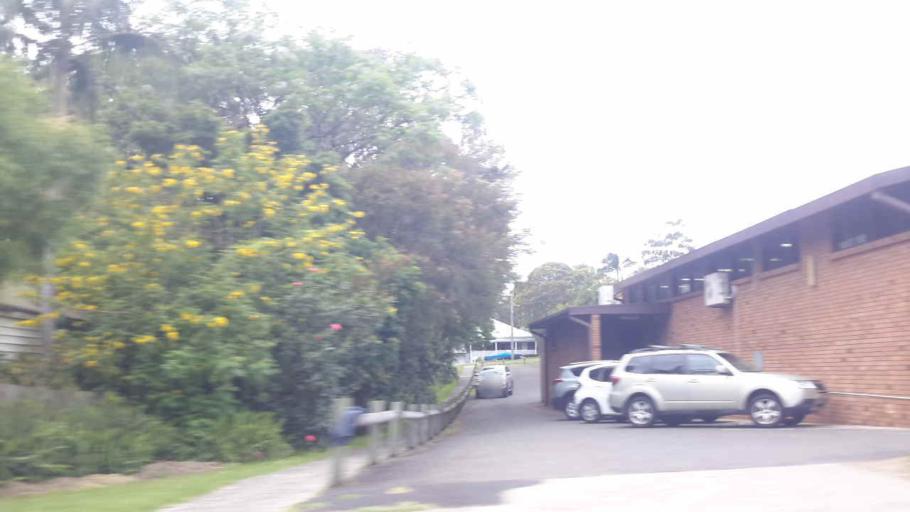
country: AU
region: New South Wales
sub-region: Wollongong
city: Bulli
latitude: -34.3449
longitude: 150.9043
